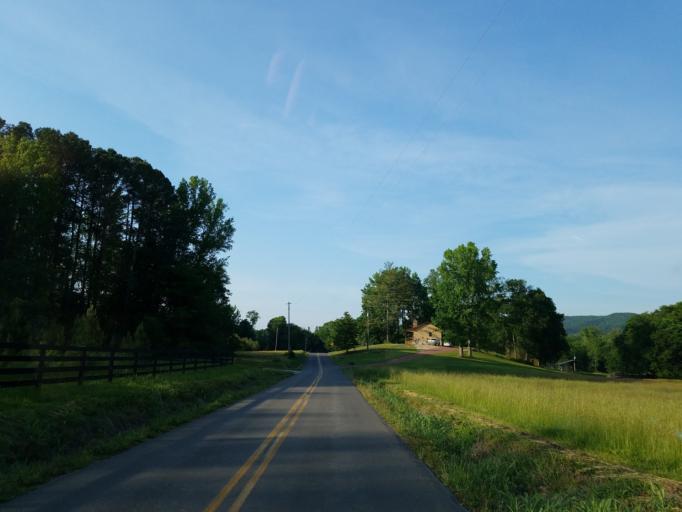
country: US
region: Georgia
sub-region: Gordon County
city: Calhoun
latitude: 34.5192
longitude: -85.1199
